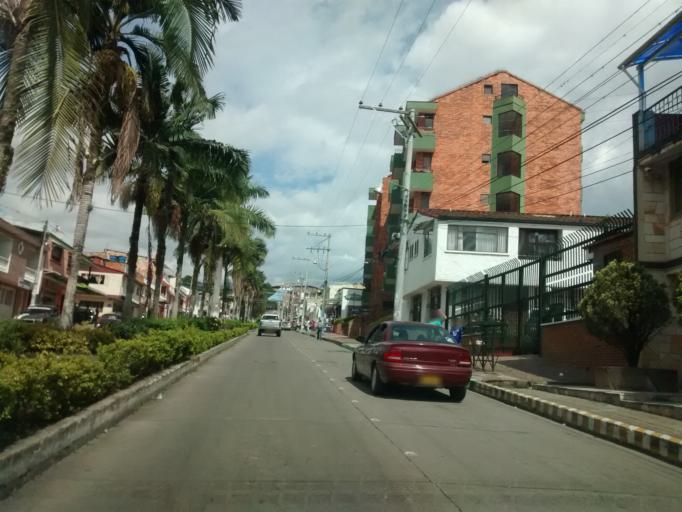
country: CO
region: Cundinamarca
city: Fusagasuga
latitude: 4.3352
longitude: -74.3650
